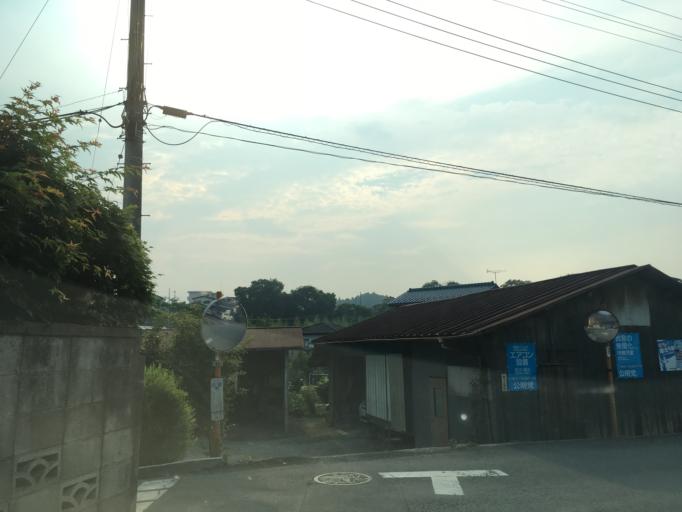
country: JP
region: Saitama
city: Chichibu
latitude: 35.9919
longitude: 139.1029
